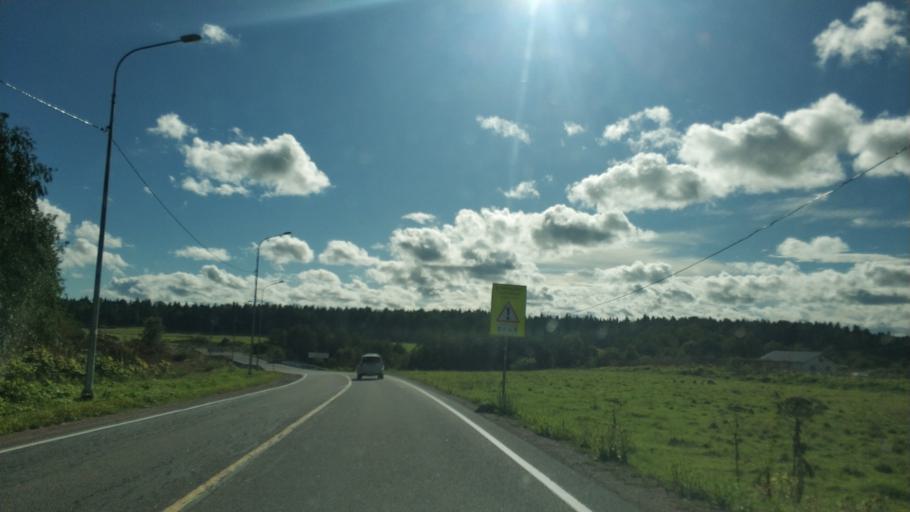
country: RU
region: Republic of Karelia
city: Khelyulya
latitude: 61.6469
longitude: 30.5848
